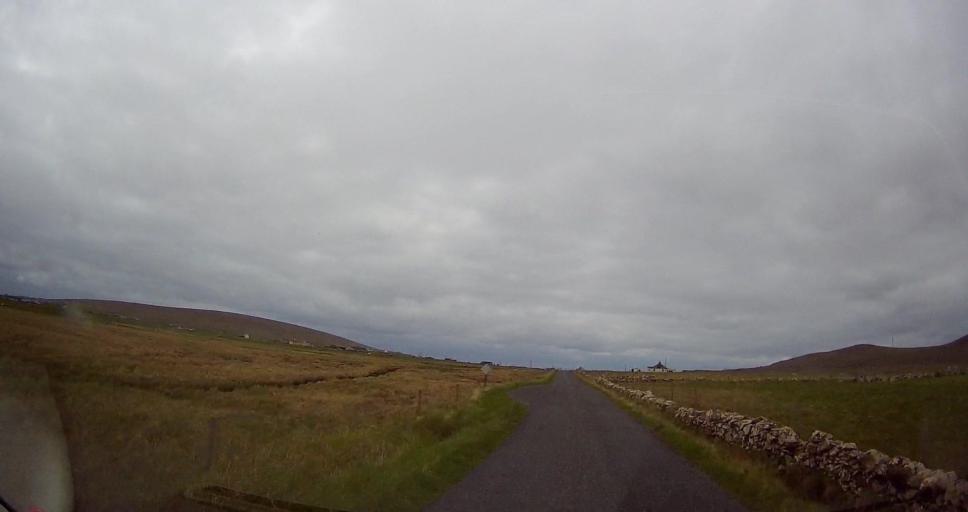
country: GB
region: Scotland
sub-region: Shetland Islands
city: Shetland
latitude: 60.7931
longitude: -0.8515
